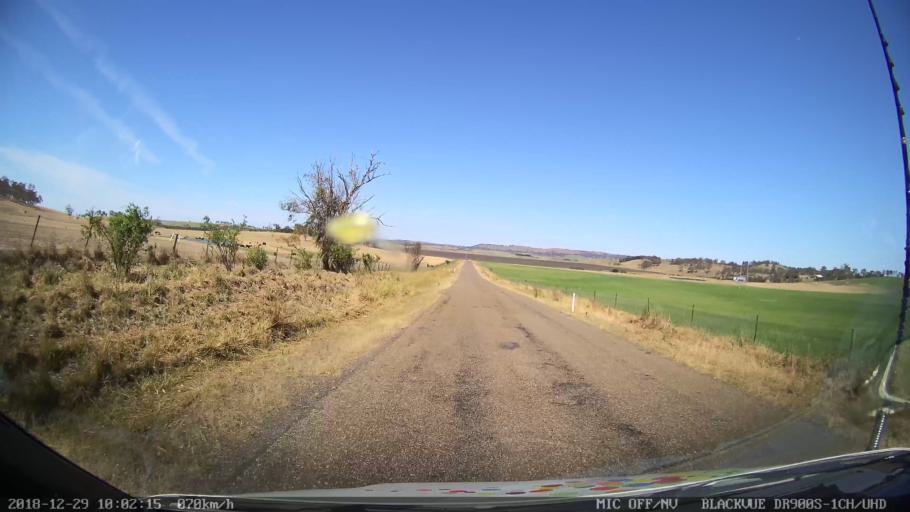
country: AU
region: New South Wales
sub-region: Goulburn Mulwaree
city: Goulburn
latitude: -34.8005
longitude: 149.4667
